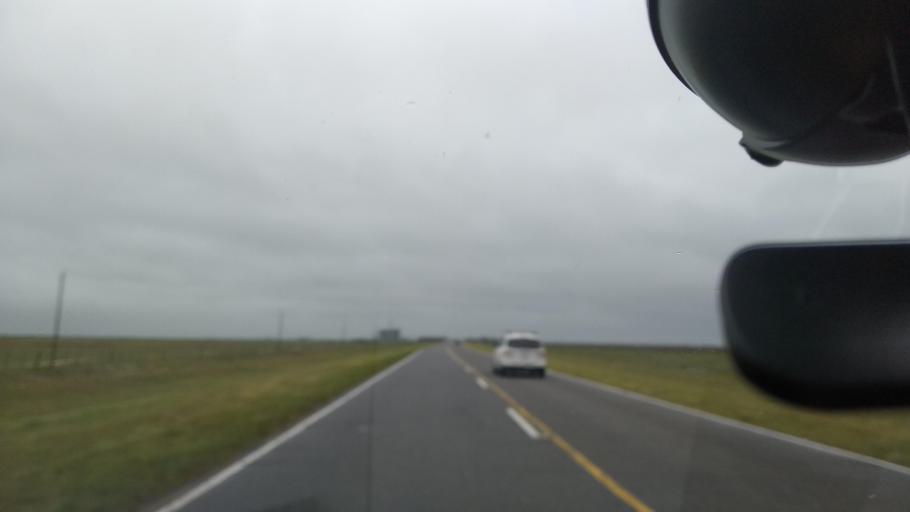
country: AR
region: Buenos Aires
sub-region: Partido de Dolores
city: Dolores
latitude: -36.0900
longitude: -57.4361
